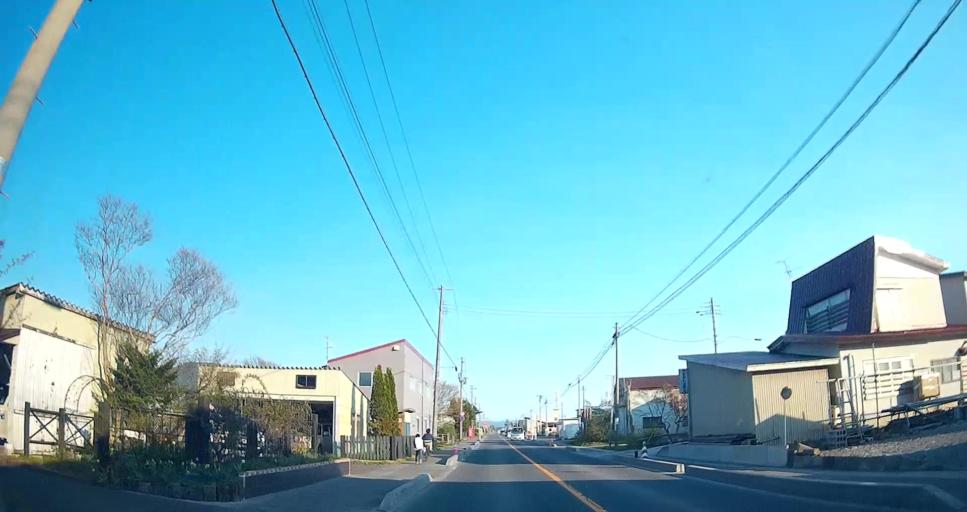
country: JP
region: Aomori
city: Mutsu
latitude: 41.2696
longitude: 141.2191
